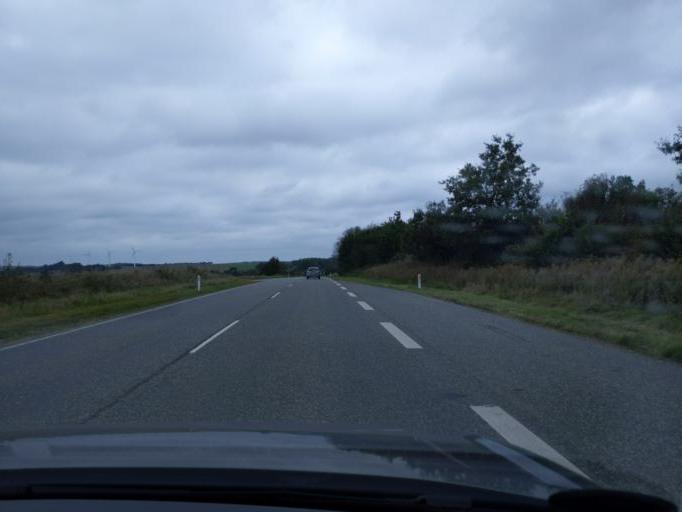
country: DK
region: North Denmark
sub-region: Mariagerfjord Kommune
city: Hobro
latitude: 56.5654
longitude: 9.8327
